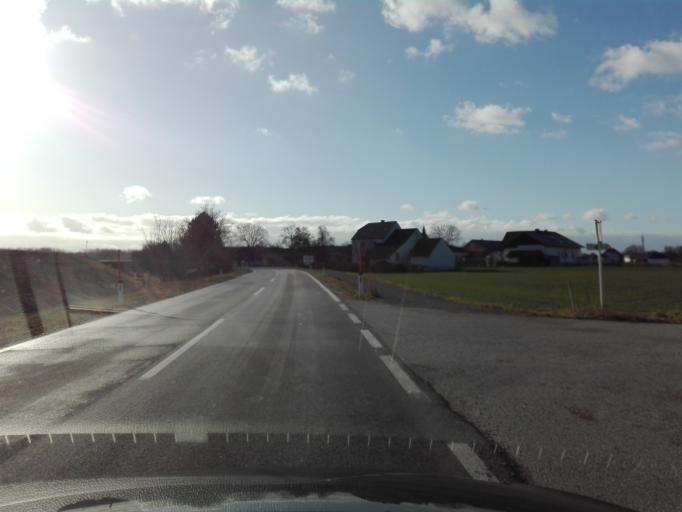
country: AT
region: Lower Austria
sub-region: Politischer Bezirk Amstetten
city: Strengberg
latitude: 48.1877
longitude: 14.7151
